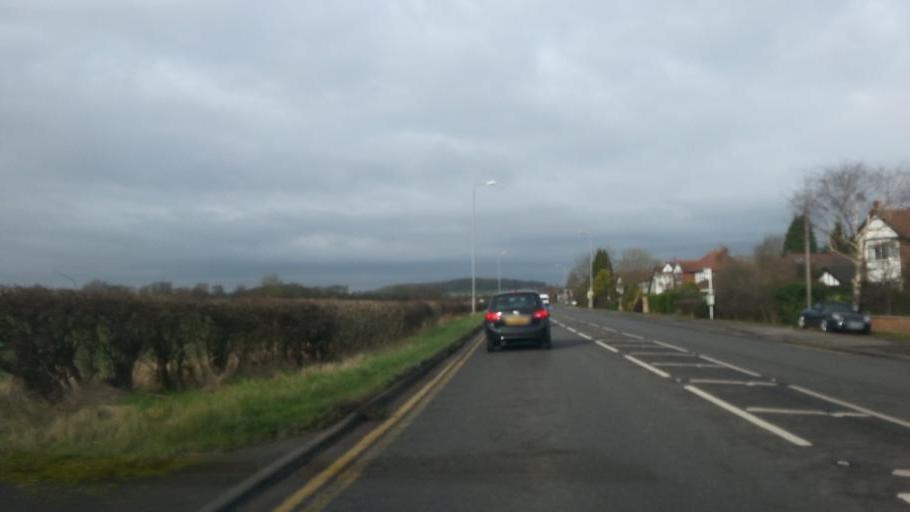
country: GB
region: England
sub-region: Nottinghamshire
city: West Bridgford
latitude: 52.8981
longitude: -1.0979
